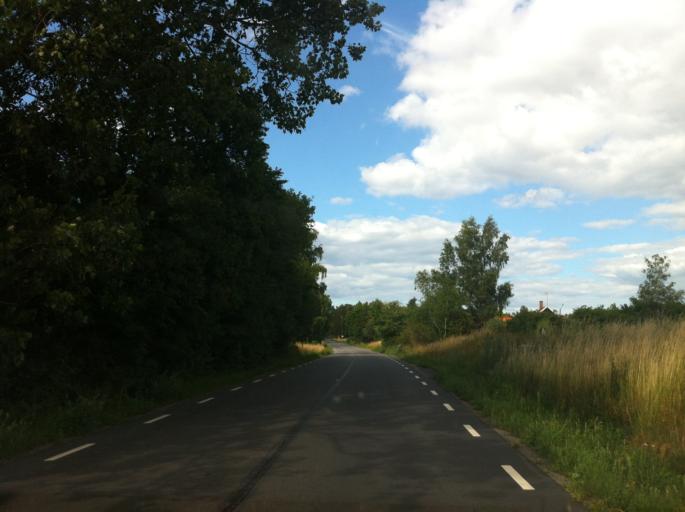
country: SE
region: Skane
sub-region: Simrishamns Kommun
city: Simrishamn
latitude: 55.4441
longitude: 14.2439
